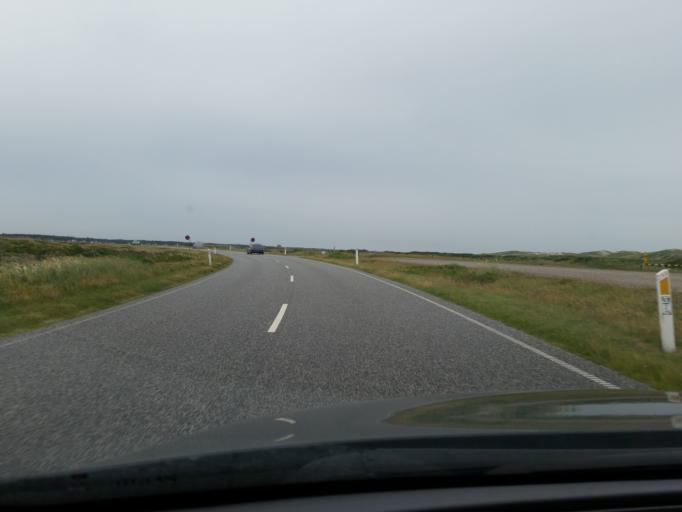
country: DK
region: Central Jutland
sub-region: Ringkobing-Skjern Kommune
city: Hvide Sande
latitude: 55.8272
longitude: 8.1728
